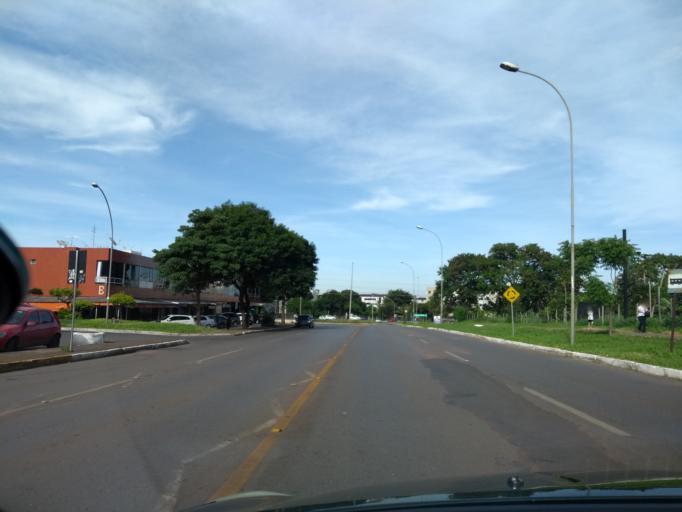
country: BR
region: Federal District
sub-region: Brasilia
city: Brasilia
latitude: -15.7965
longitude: -47.9317
